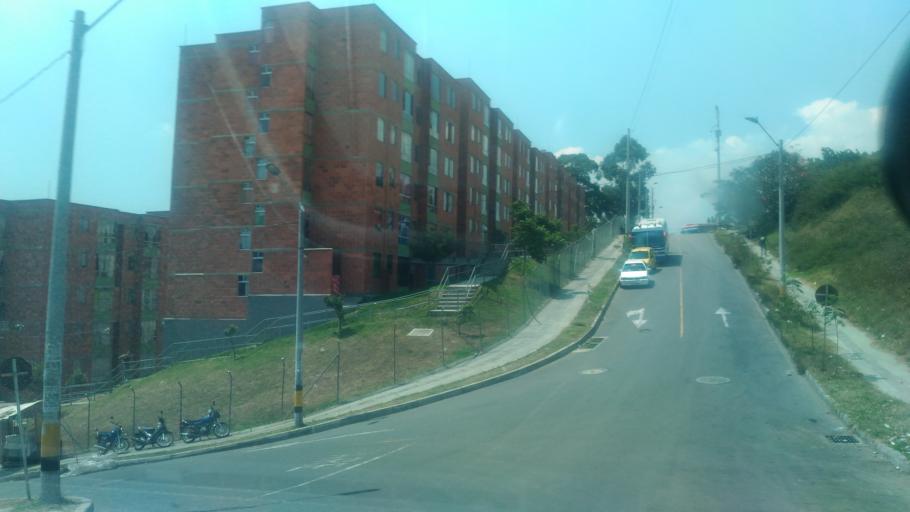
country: CO
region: Antioquia
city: Medellin
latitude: 6.2945
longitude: -75.5876
